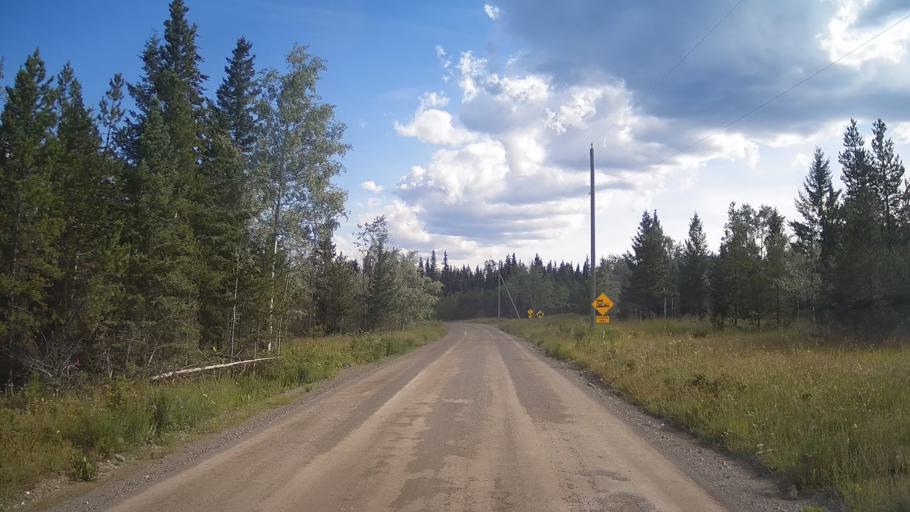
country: CA
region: British Columbia
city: Cache Creek
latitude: 51.1837
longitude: -121.5838
